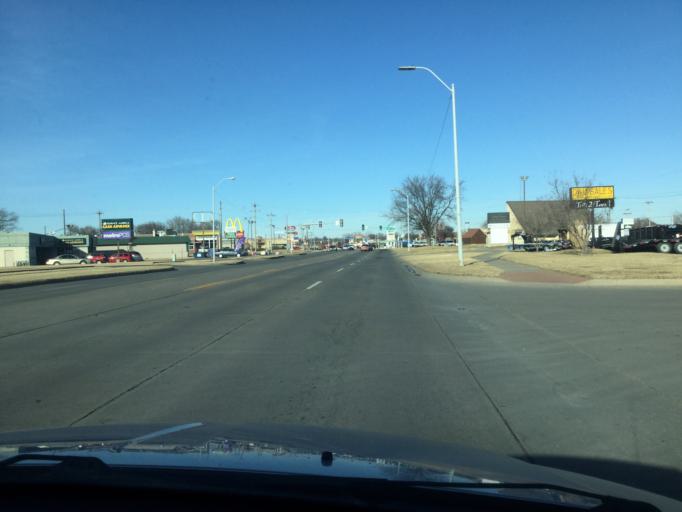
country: US
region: Kansas
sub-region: Shawnee County
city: Topeka
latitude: 39.0834
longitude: -95.6659
